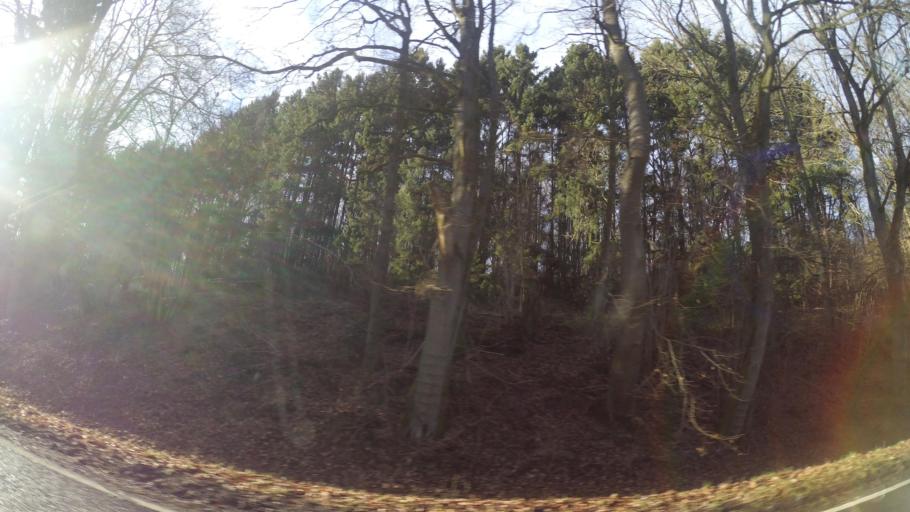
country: DE
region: Rheinland-Pfalz
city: Blaubach
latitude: 49.5633
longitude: 7.4023
